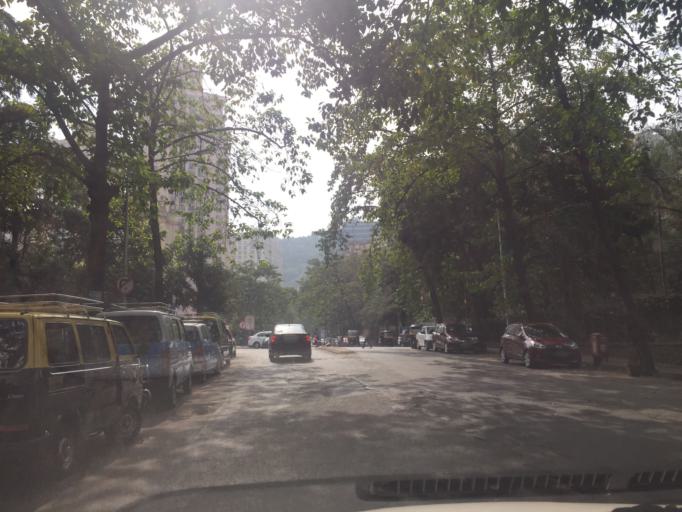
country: IN
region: Maharashtra
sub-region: Mumbai Suburban
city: Powai
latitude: 19.1161
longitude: 72.9081
